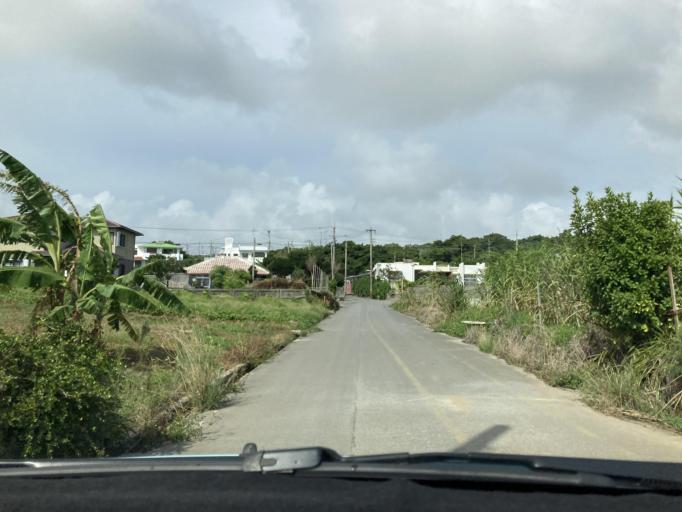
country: JP
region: Okinawa
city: Itoman
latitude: 26.0937
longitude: 127.7044
